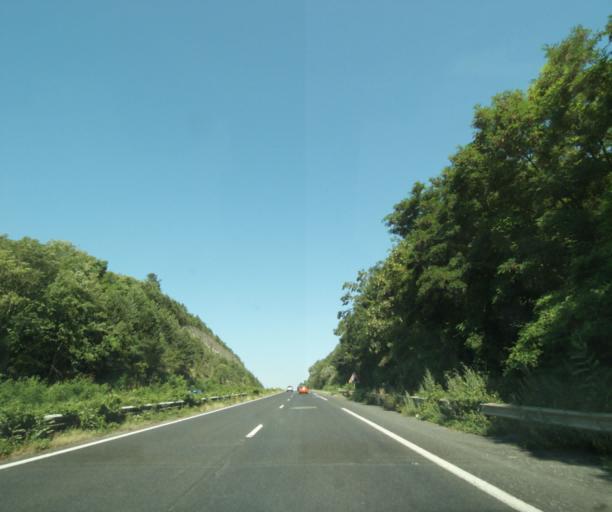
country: FR
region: Lorraine
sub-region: Departement de Meurthe-et-Moselle
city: Foug
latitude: 48.6735
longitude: 5.7728
